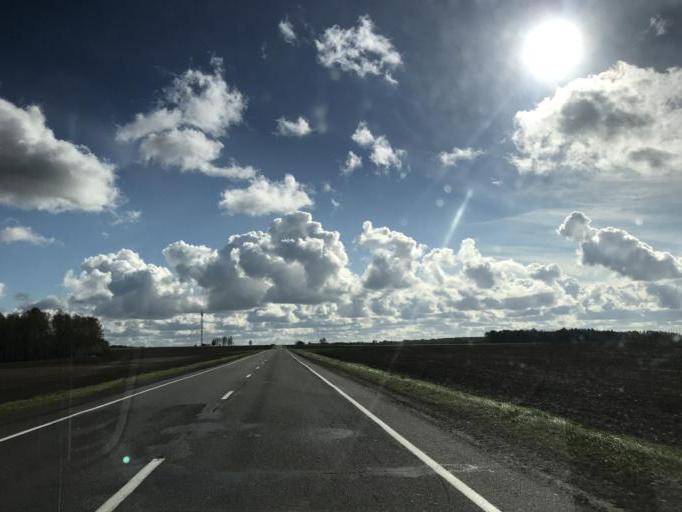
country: BY
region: Gomel
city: Buda-Kashalyova
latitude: 52.8075
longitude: 30.7301
